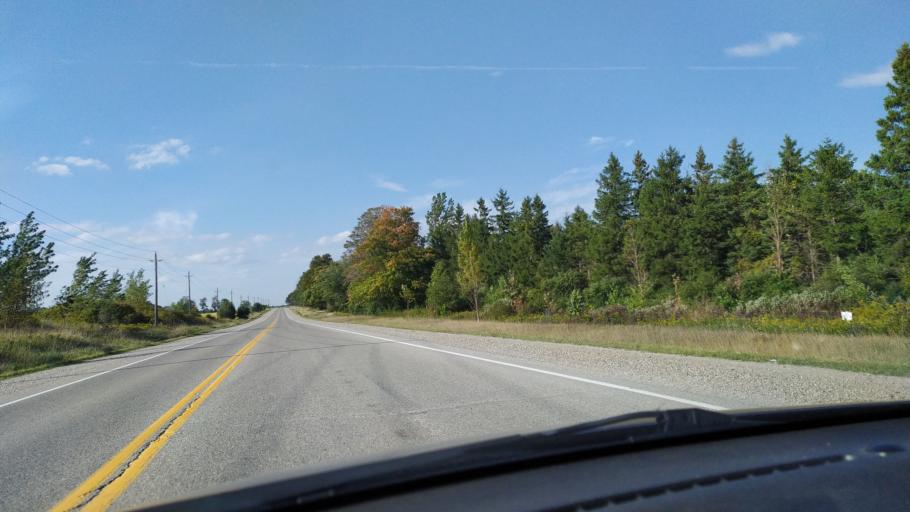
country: CA
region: Ontario
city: Ingersoll
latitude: 43.0787
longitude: -80.8614
